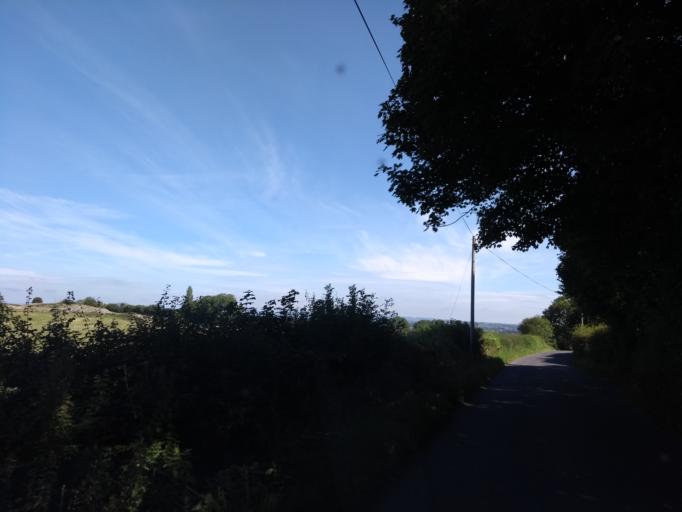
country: GB
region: England
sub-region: Somerset
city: Ilchester
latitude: 51.0784
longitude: -2.6449
